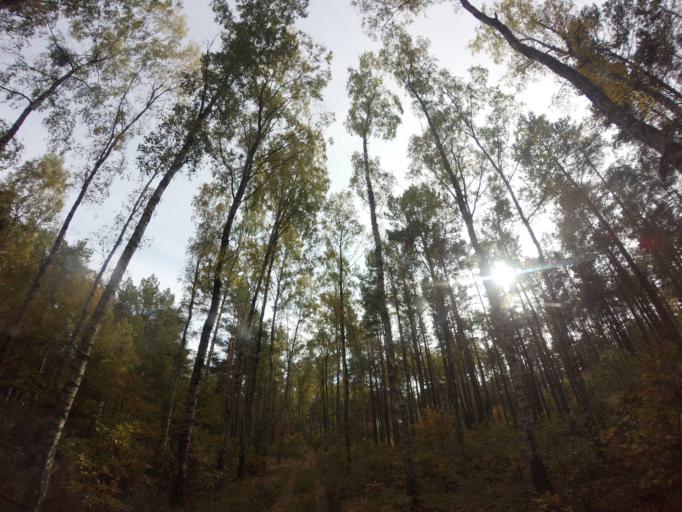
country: PL
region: West Pomeranian Voivodeship
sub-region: Powiat choszczenski
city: Drawno
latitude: 53.2455
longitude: 15.6834
